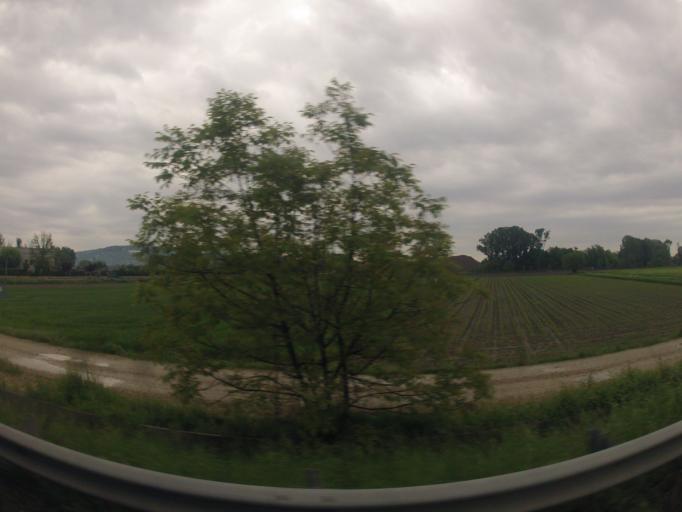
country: IT
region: Piedmont
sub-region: Provincia di Torino
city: La Loggia
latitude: 44.9640
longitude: 7.6769
